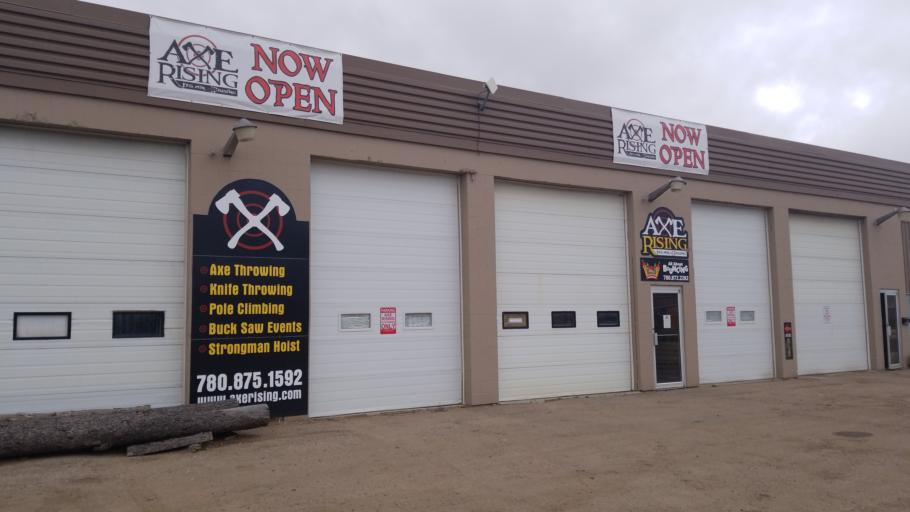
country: CA
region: Saskatchewan
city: Lloydminster
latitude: 53.2822
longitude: -110.0345
